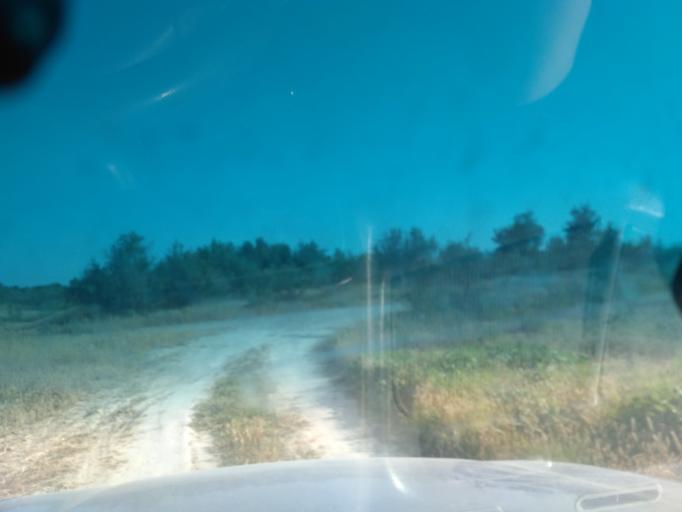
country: TJ
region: Viloyati Sughd
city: Buston
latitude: 40.5588
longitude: 69.0763
